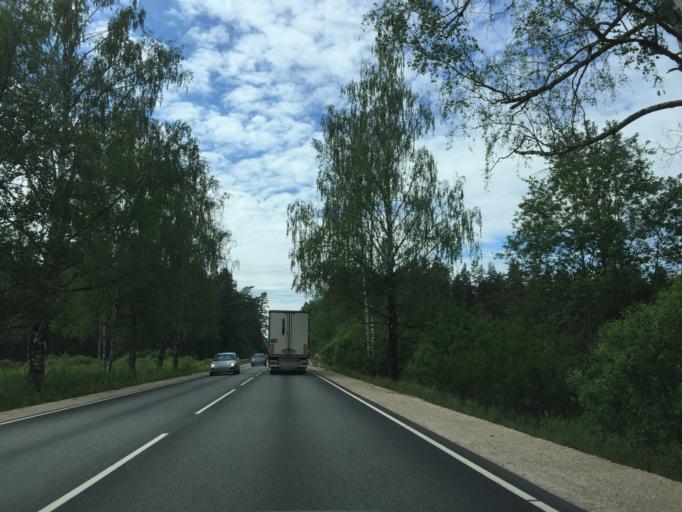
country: LV
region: Ikskile
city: Ikskile
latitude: 56.8878
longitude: 24.4872
